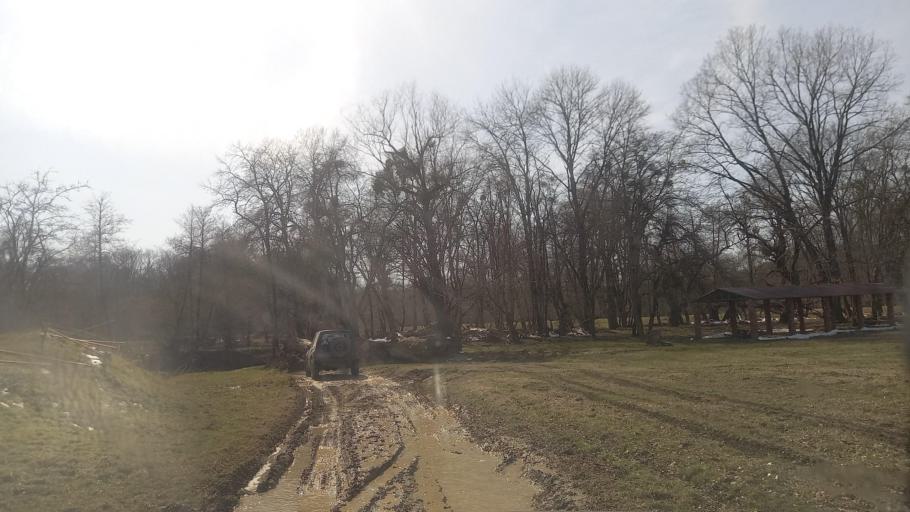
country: RU
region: Krasnodarskiy
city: Smolenskaya
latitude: 44.6011
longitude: 38.8501
